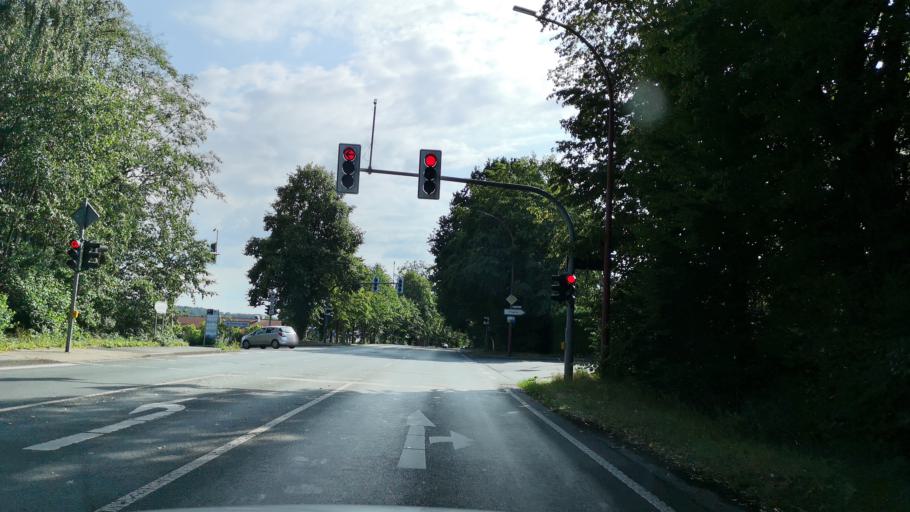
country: DE
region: North Rhine-Westphalia
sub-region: Regierungsbezirk Arnsberg
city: Holzwickede
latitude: 51.4579
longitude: 7.6138
